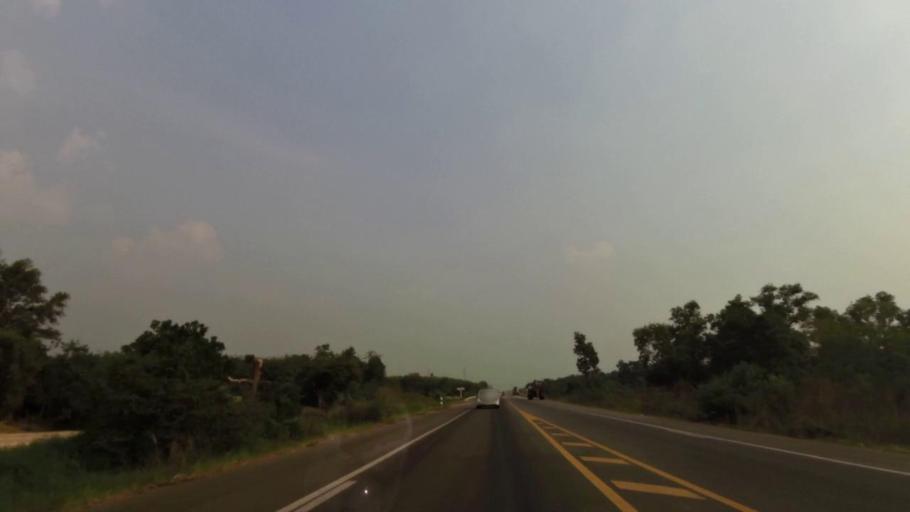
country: TH
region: Rayong
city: Klaeng
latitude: 12.8069
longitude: 101.6504
